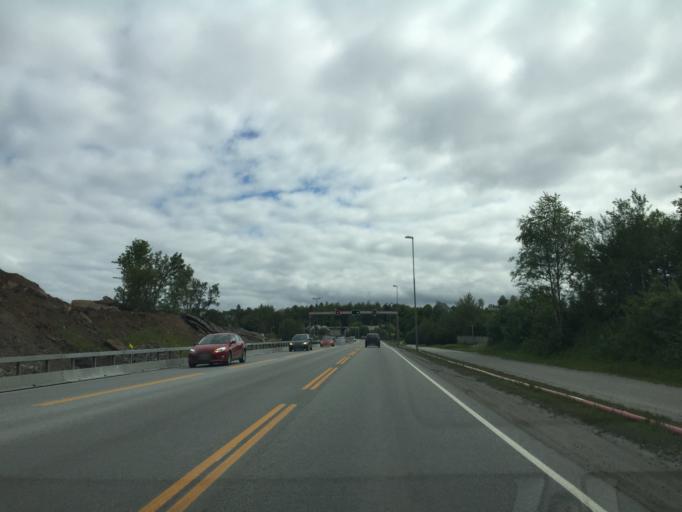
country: NO
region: Nordland
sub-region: Bodo
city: Bodo
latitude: 67.2773
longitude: 14.4355
